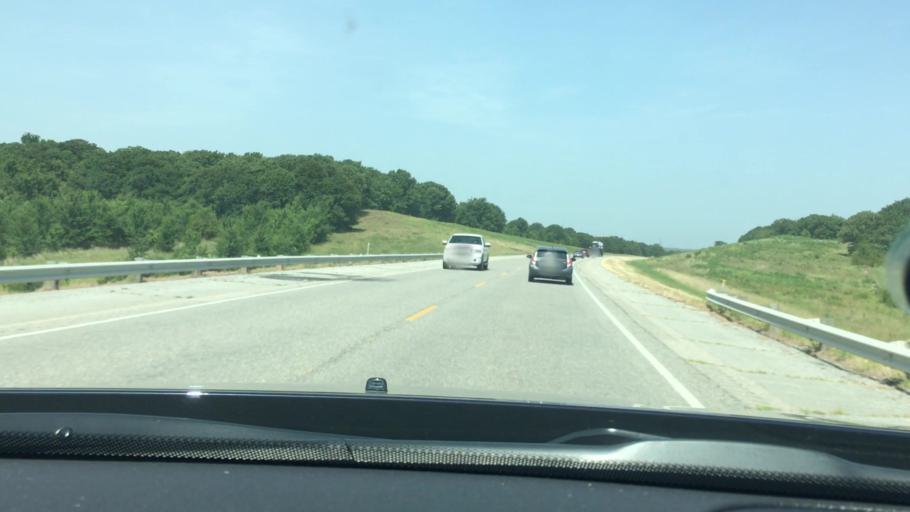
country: US
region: Oklahoma
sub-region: Coal County
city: Coalgate
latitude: 34.6005
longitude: -96.3634
